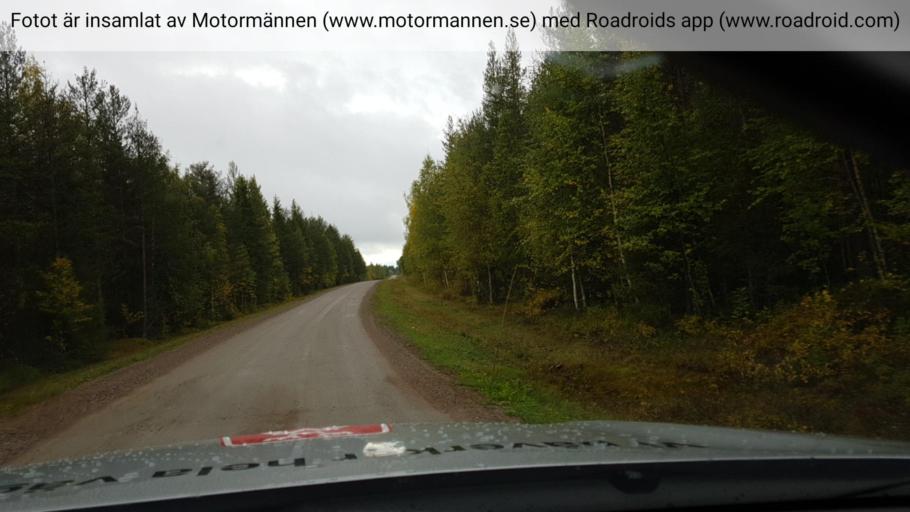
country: SE
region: Norrbotten
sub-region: Alvsbyns Kommun
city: AElvsbyn
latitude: 66.1966
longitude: 20.8429
